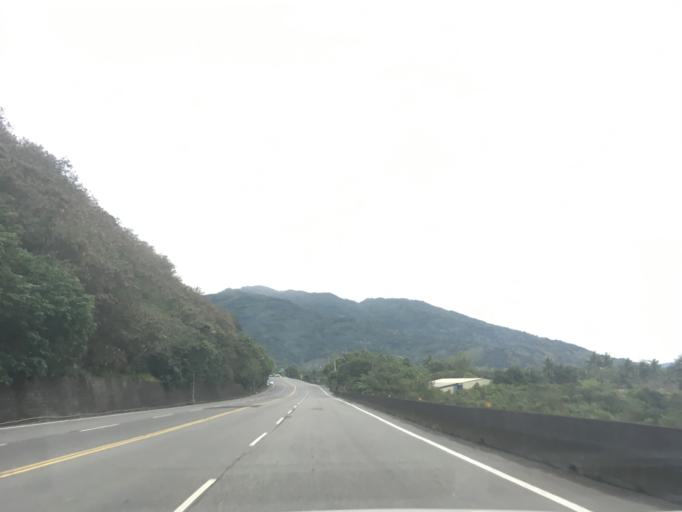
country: TW
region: Taiwan
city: Taitung City
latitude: 22.7506
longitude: 121.0543
